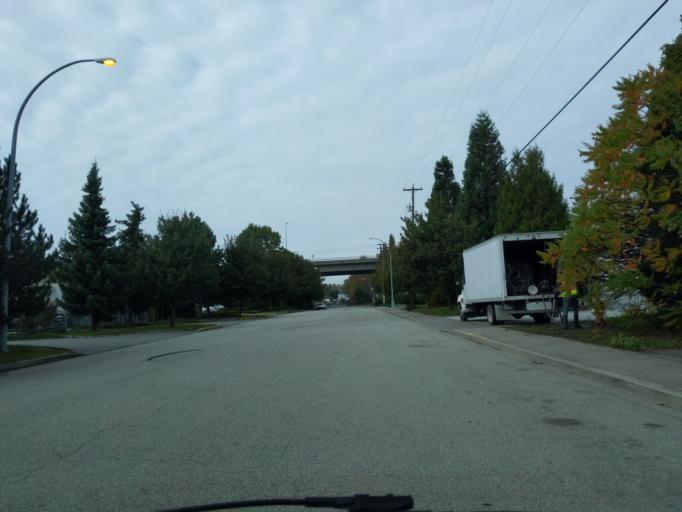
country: CA
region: British Columbia
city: Walnut Grove
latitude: 49.1875
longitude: -122.6617
